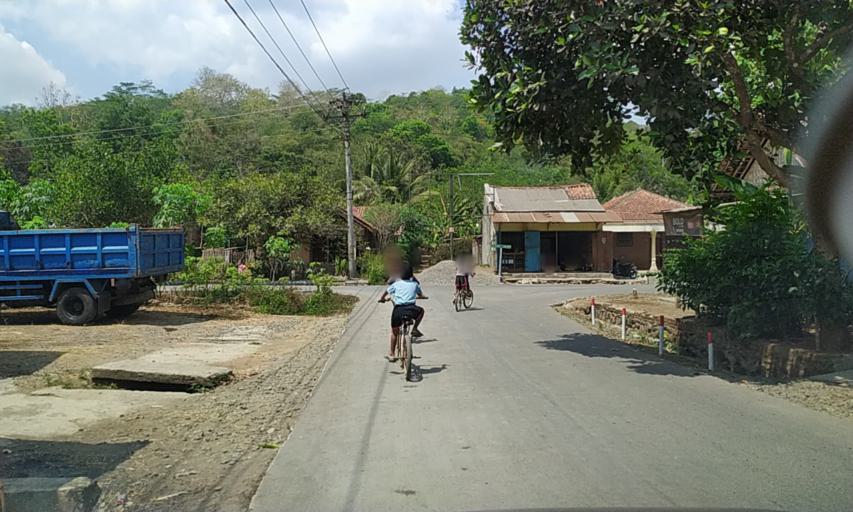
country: ID
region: Central Java
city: Tawangsari
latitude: -7.3922
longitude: 108.7975
